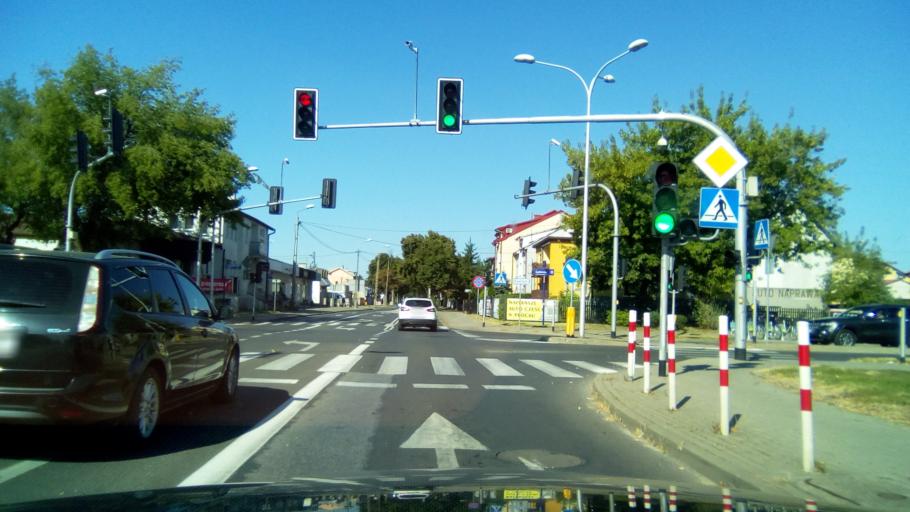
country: PL
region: Masovian Voivodeship
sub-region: Plock
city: Plock
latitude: 52.5394
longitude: 19.7174
